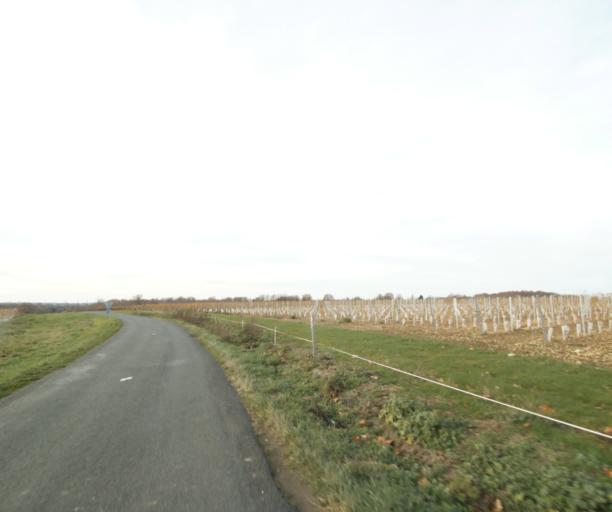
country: FR
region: Poitou-Charentes
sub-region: Departement de la Charente-Maritime
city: Saint-Hilaire-de-Villefranche
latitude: 45.8173
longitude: -0.5473
